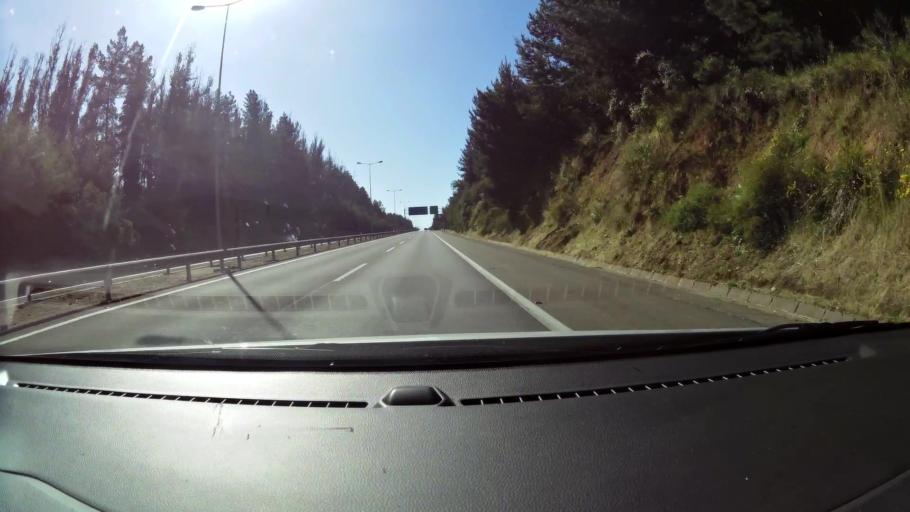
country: CL
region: Valparaiso
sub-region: Provincia de Valparaiso
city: Vina del Mar
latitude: -33.1649
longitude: -71.5347
